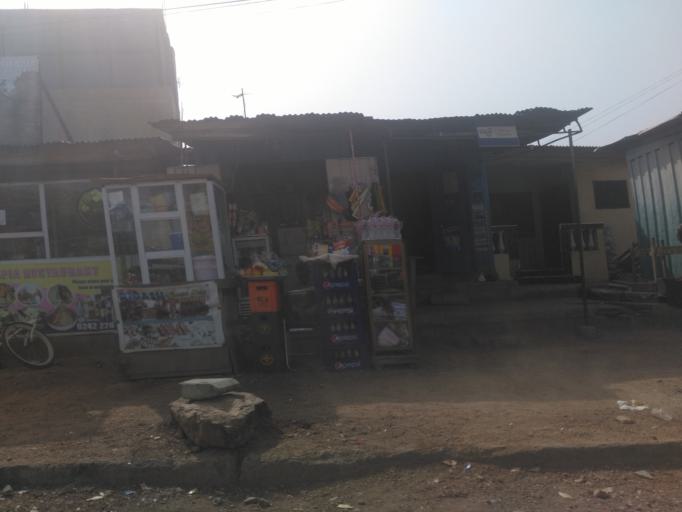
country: GH
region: Greater Accra
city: Gbawe
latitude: 5.5798
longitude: -0.2643
